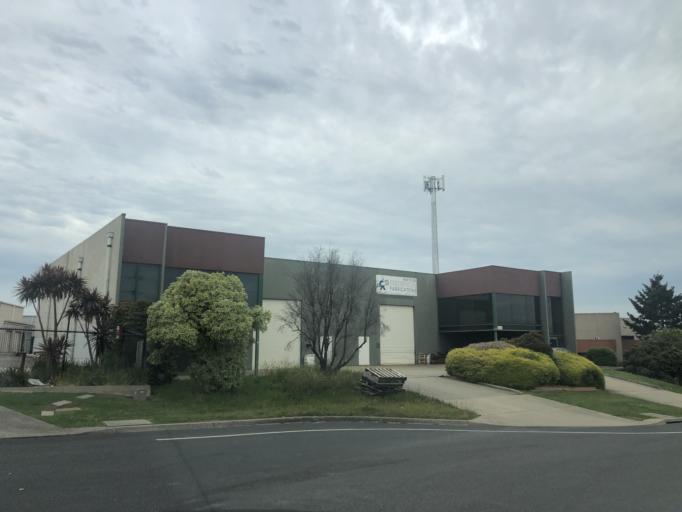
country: AU
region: Victoria
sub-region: Casey
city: Hallam
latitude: -38.0089
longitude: 145.2682
